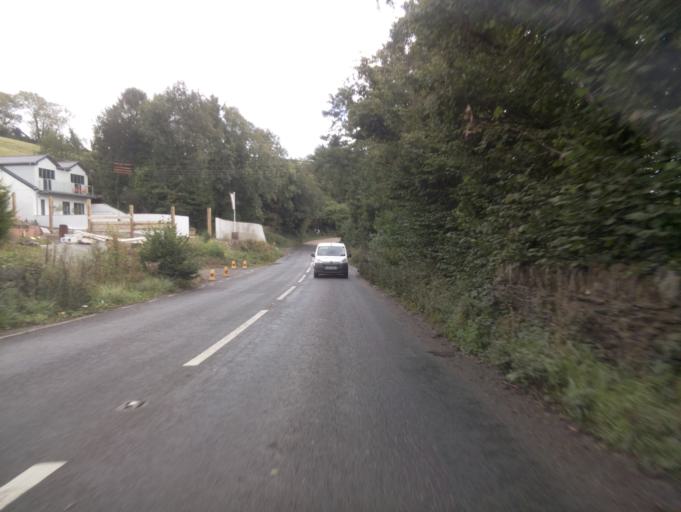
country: GB
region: England
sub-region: Devon
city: Modbury
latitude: 50.3277
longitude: -3.8425
